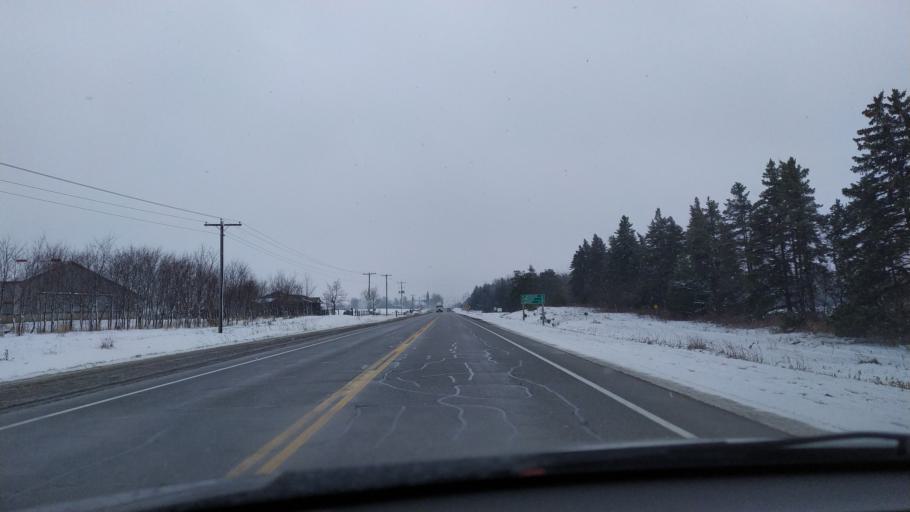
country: CA
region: Ontario
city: Waterloo
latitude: 43.6264
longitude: -80.7014
